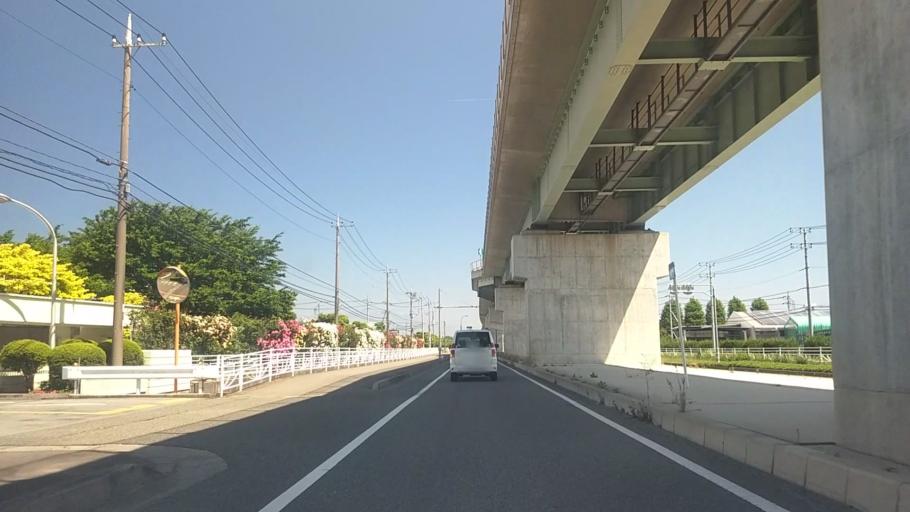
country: JP
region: Yamanashi
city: Ryuo
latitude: 35.5798
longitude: 138.4751
